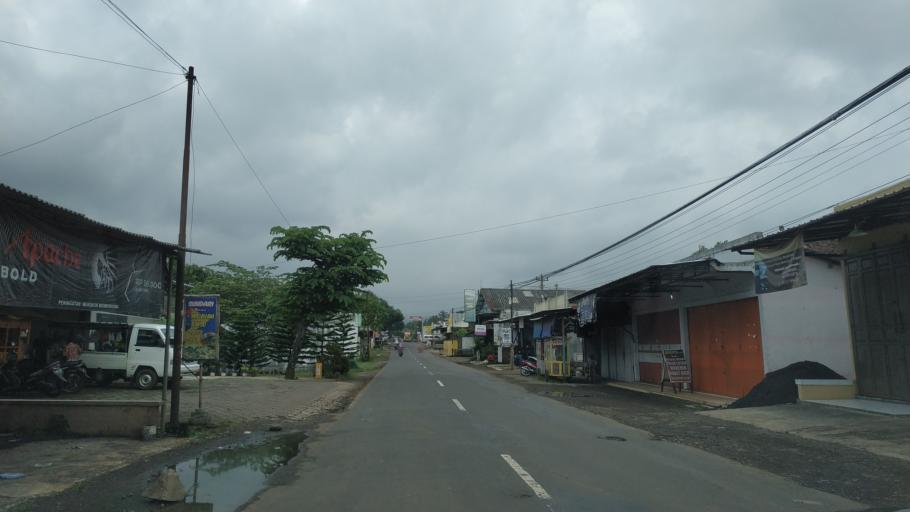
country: ID
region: Central Java
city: Weleri
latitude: -7.0788
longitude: 110.0437
